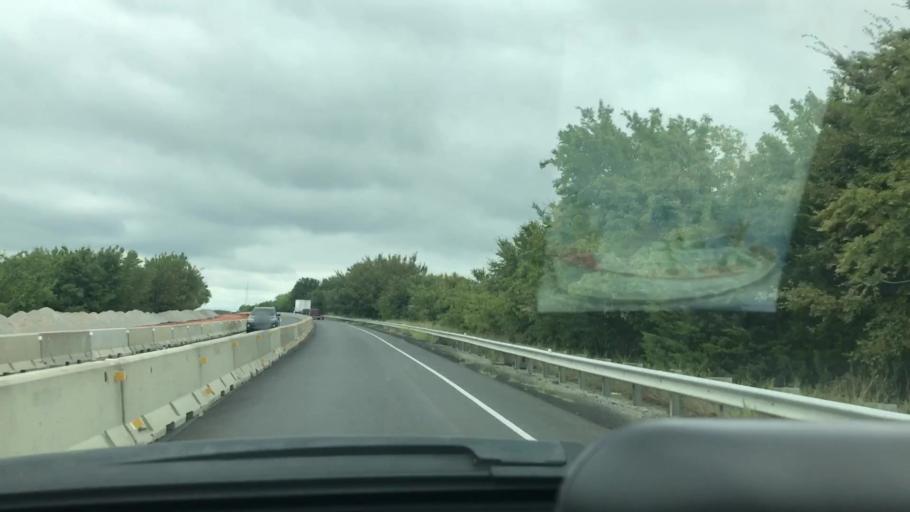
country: US
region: Oklahoma
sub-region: McIntosh County
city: Eufaula
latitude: 35.2503
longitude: -95.5851
